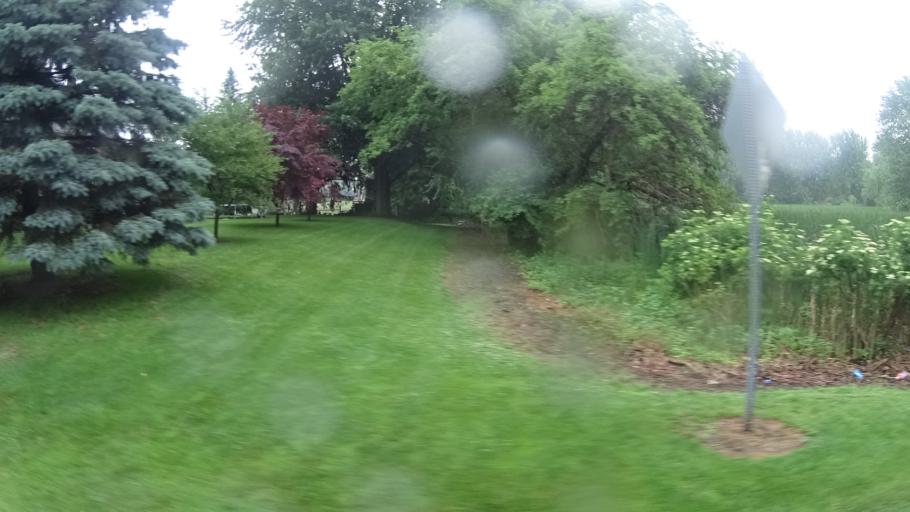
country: US
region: Ohio
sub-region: Huron County
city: Bellevue
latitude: 41.3708
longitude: -82.8450
